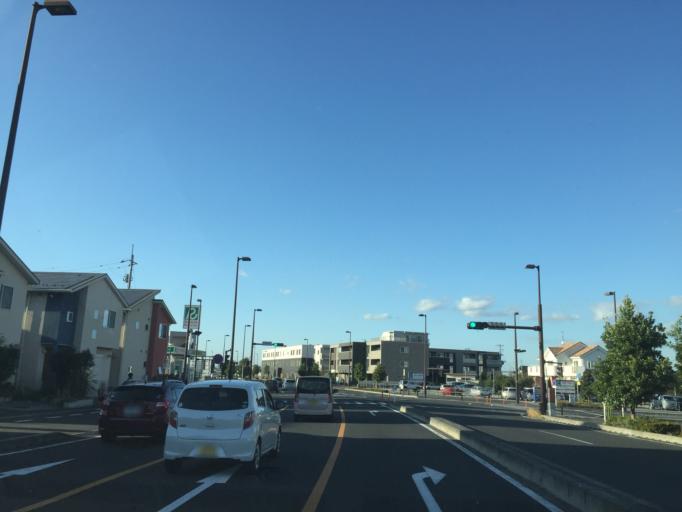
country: JP
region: Saitama
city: Koshigaya
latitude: 35.8929
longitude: 139.7262
